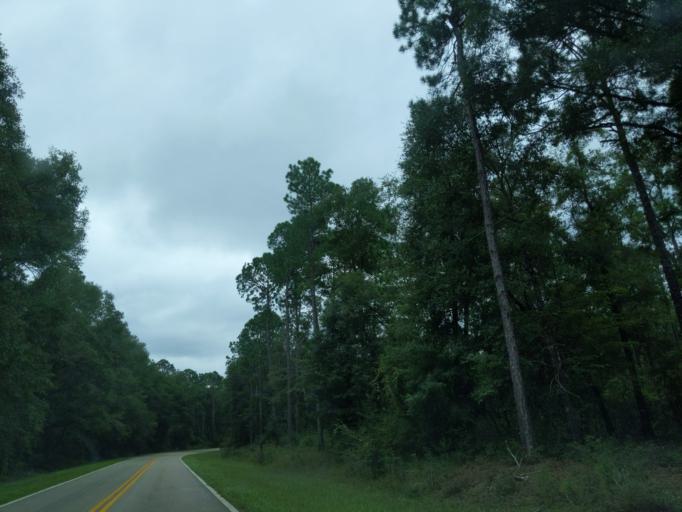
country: US
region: Florida
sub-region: Gadsden County
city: Midway
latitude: 30.4064
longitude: -84.4150
